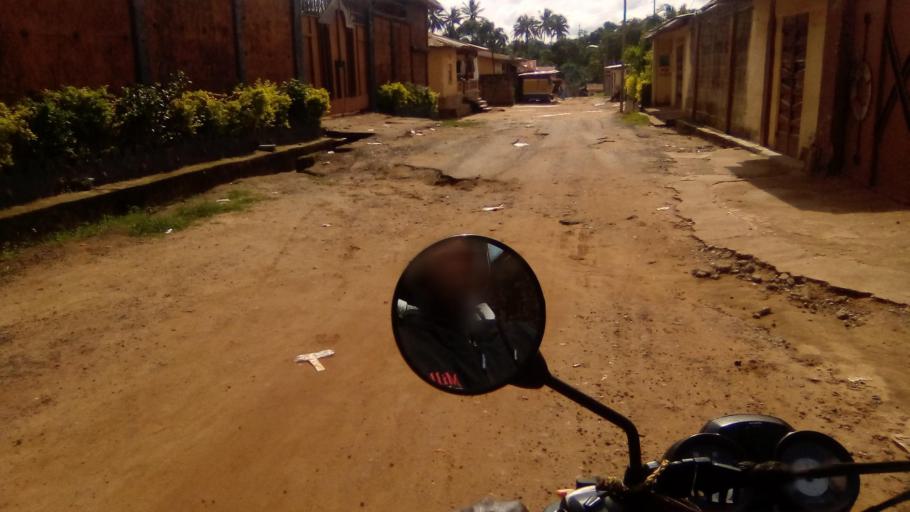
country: SL
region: Southern Province
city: Bo
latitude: 7.9569
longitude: -11.7526
